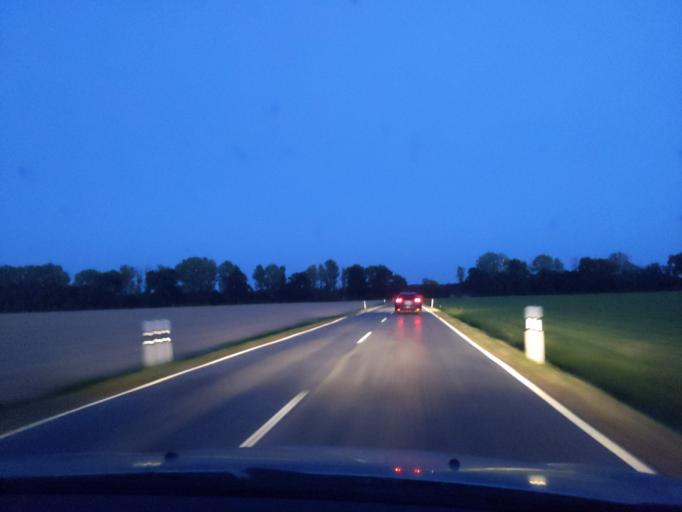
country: DE
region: Saxony
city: Guttau
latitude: 51.2556
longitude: 14.5360
